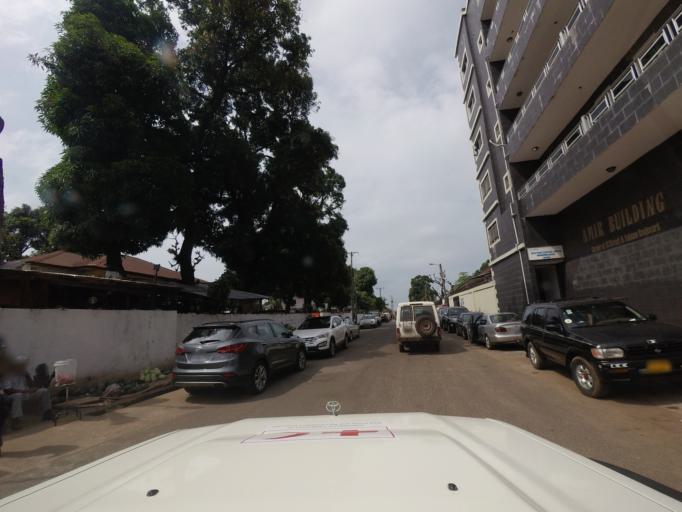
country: LR
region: Montserrado
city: Monrovia
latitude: 6.2905
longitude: -10.7763
